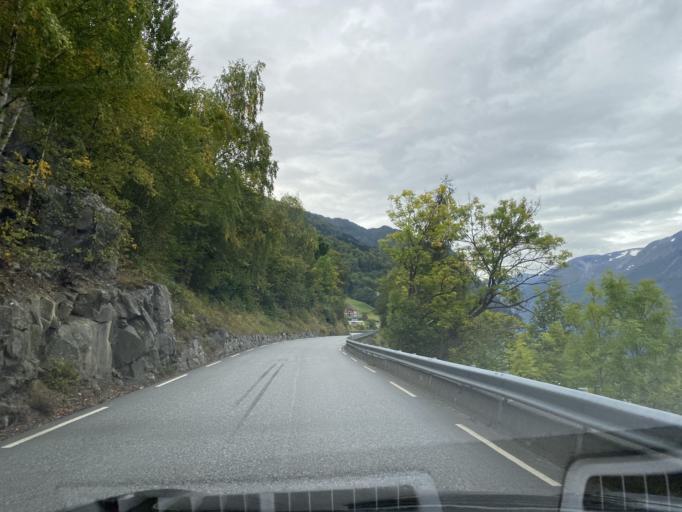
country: NO
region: Hordaland
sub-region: Odda
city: Odda
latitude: 60.2109
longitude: 6.6021
